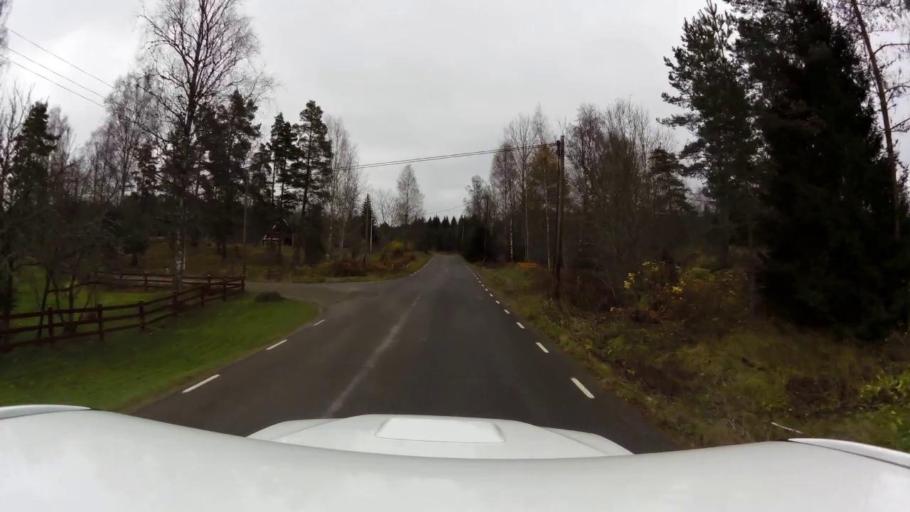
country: SE
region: OEstergoetland
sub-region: Kinda Kommun
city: Rimforsa
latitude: 58.1449
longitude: 15.4593
